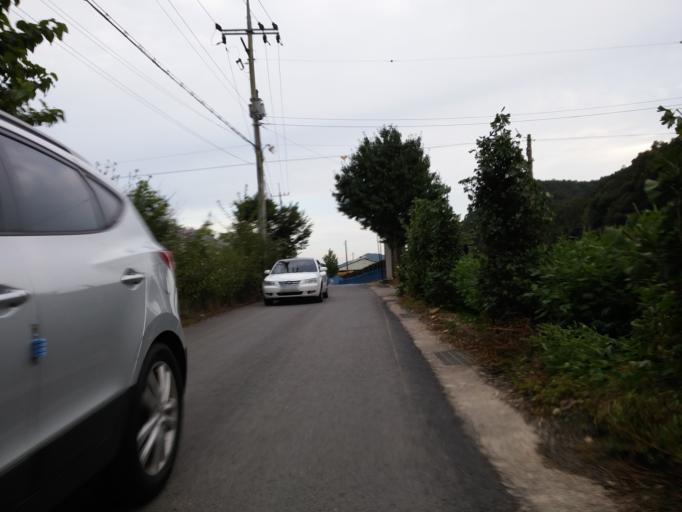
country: KR
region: Daejeon
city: Daejeon
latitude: 36.2657
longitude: 127.3327
